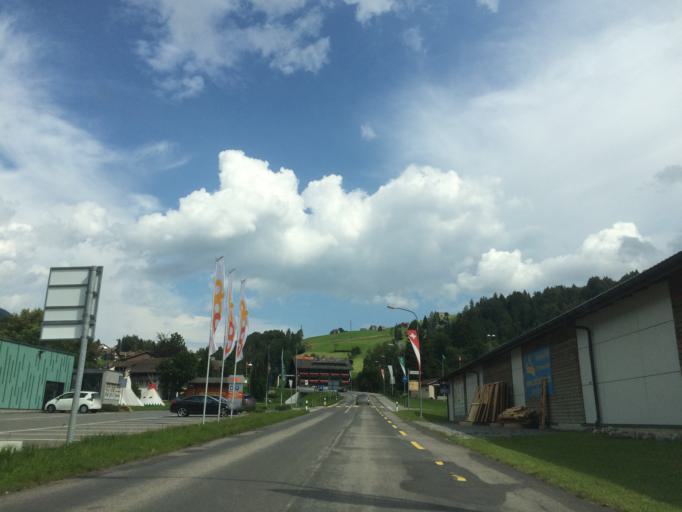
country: CH
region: Saint Gallen
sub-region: Wahlkreis Toggenburg
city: Wildhaus
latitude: 47.1965
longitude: 9.3098
